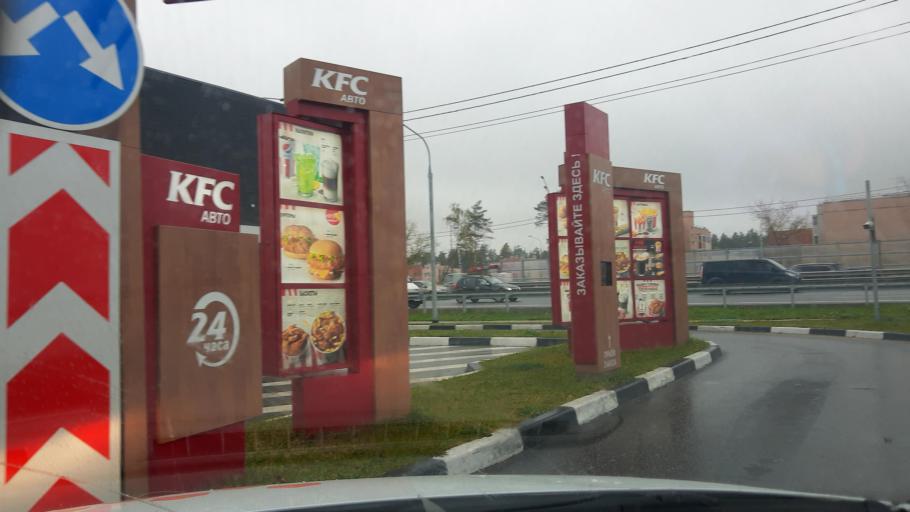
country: RU
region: Moskovskaya
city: Chornaya
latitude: 55.8072
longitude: 38.0608
